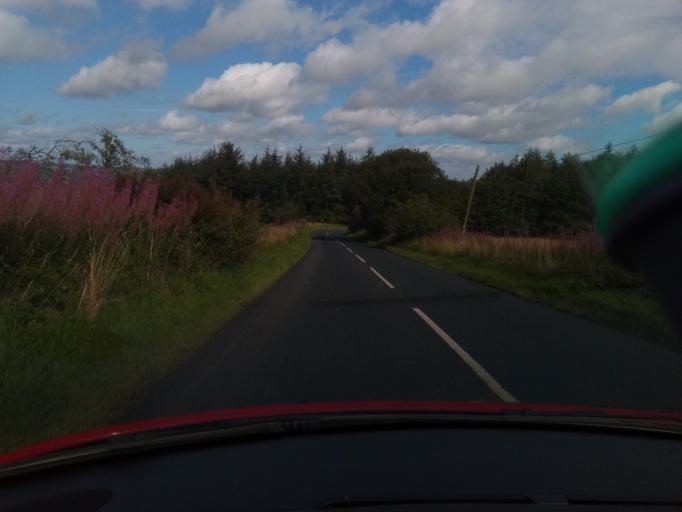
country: GB
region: Scotland
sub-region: The Scottish Borders
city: Melrose
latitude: 55.5818
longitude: -2.7364
